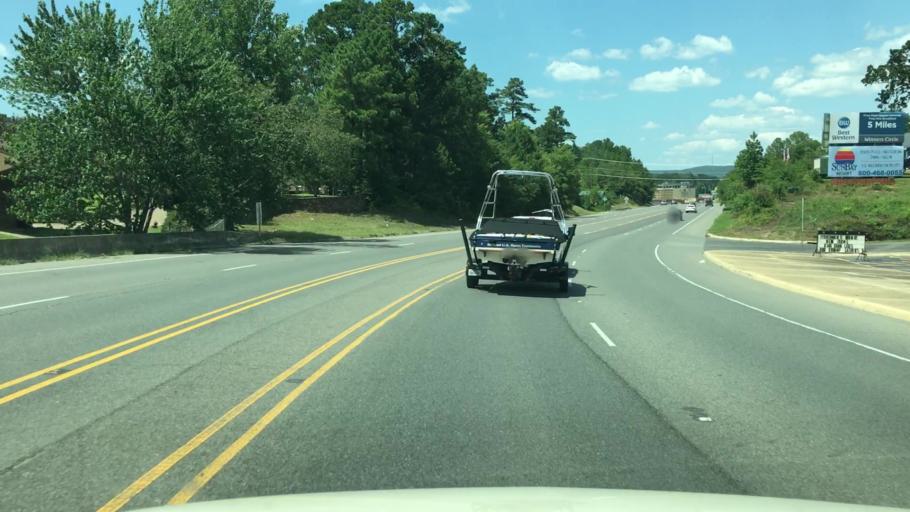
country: US
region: Arkansas
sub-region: Garland County
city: Lake Hamilton
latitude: 34.4349
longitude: -93.0885
